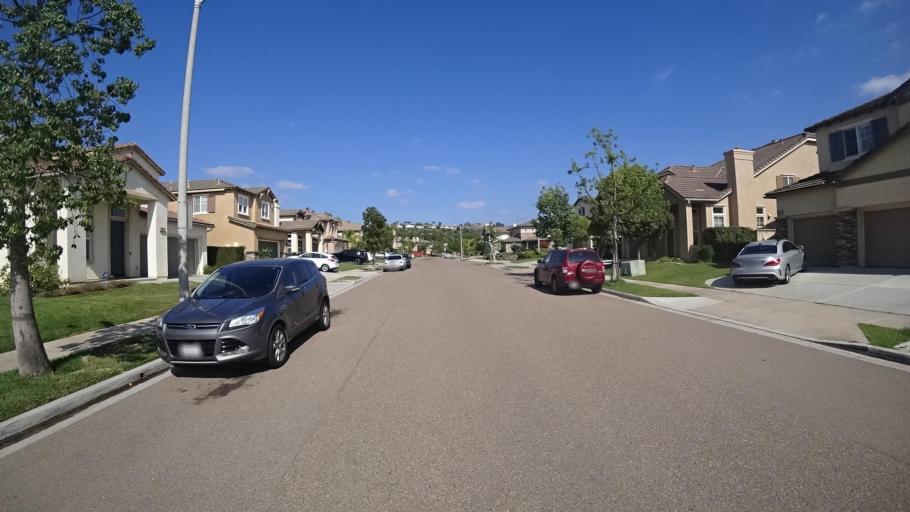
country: US
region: California
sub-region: San Diego County
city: Fairbanks Ranch
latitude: 33.0060
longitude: -117.1141
